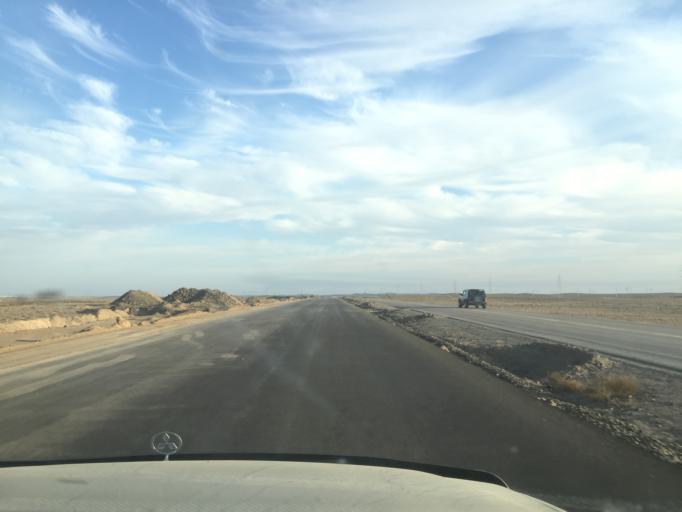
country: KZ
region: Almaty Oblysy
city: Ulken
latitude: 45.2270
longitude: 73.8495
